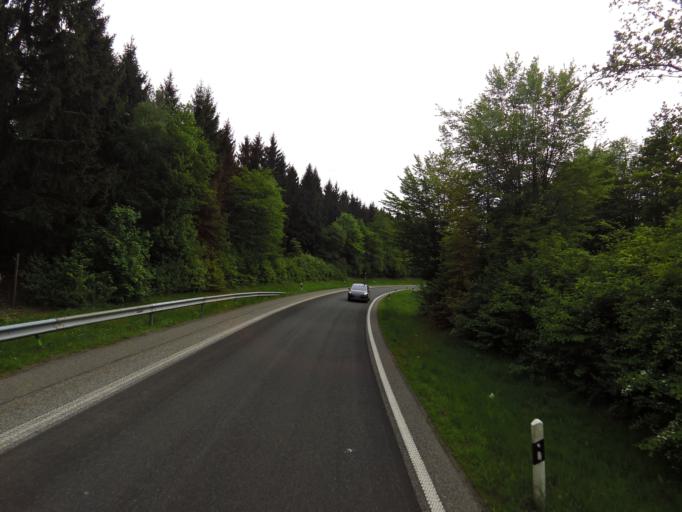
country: DE
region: Rheinland-Pfalz
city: Nortershausen
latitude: 50.2452
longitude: 7.5178
